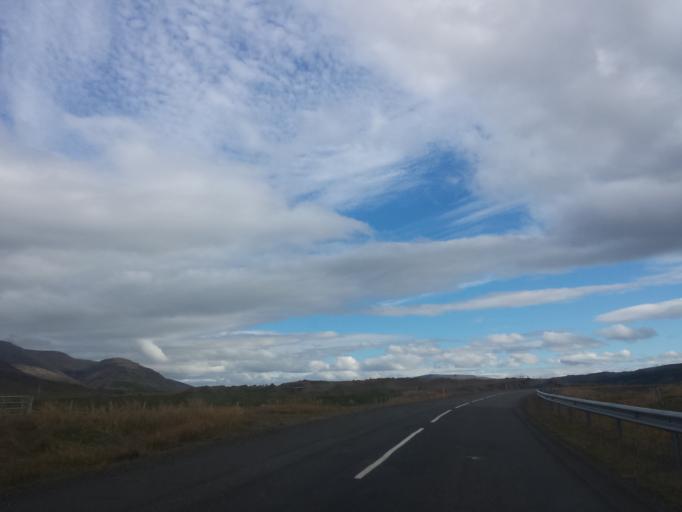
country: IS
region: West
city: Borgarnes
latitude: 64.4234
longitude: -21.7729
